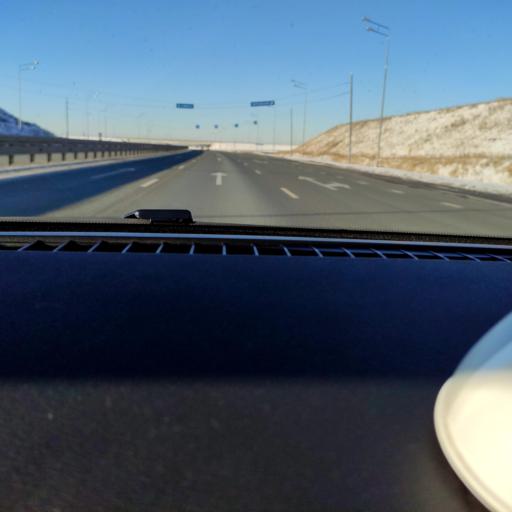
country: RU
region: Samara
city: Smyshlyayevka
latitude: 53.1473
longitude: 50.4022
